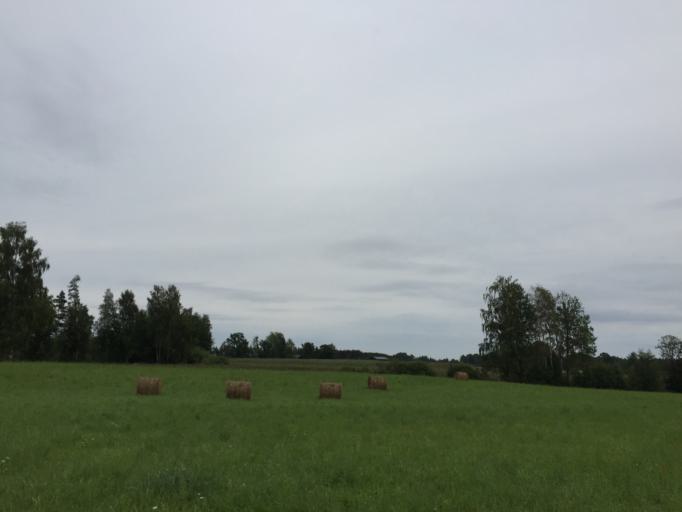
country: LV
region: Jaunpils
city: Jaunpils
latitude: 56.7282
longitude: 23.1551
